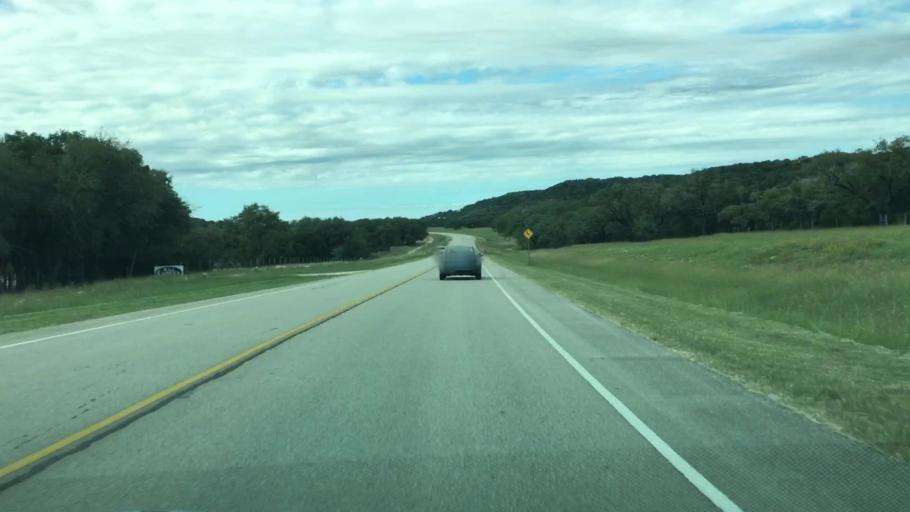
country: US
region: Texas
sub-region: Hays County
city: Wimberley
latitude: 30.0117
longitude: -98.0844
